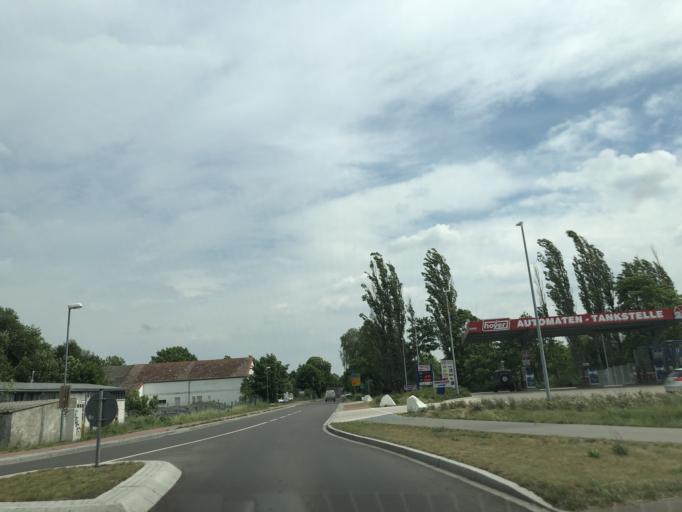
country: DE
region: Brandenburg
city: Walsleben
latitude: 52.8768
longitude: 12.6226
